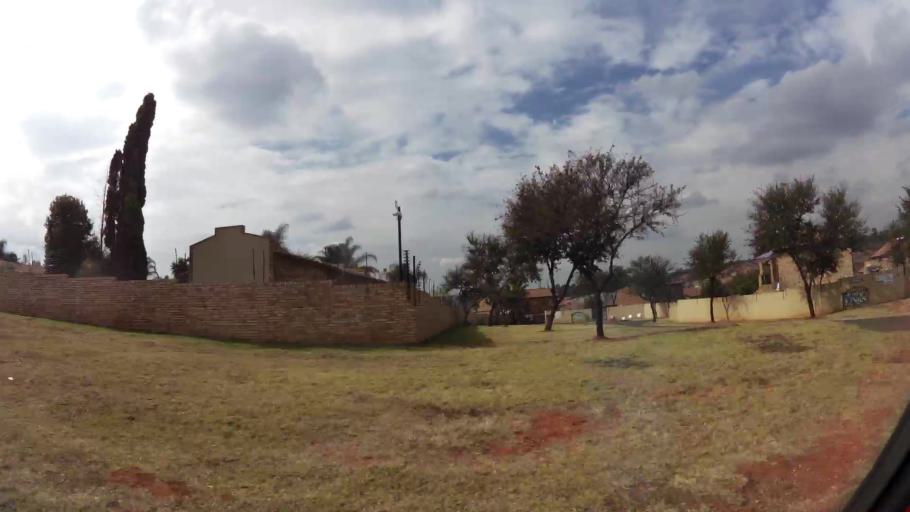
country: ZA
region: Gauteng
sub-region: City of Johannesburg Metropolitan Municipality
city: Roodepoort
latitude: -26.1017
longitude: 27.8861
